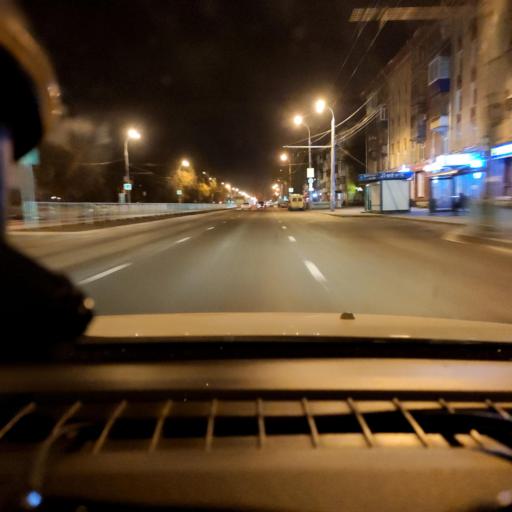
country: RU
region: Samara
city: Samara
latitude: 53.2068
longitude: 50.2356
